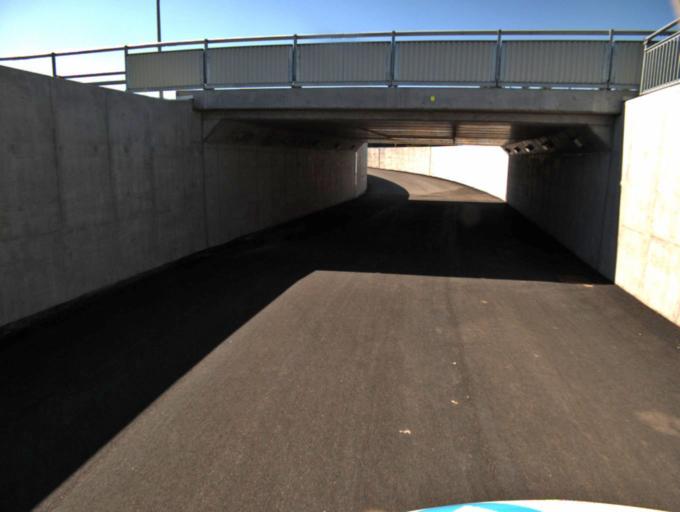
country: SE
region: Skane
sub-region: Kristianstads Kommun
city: Kristianstad
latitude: 56.0240
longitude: 14.1922
